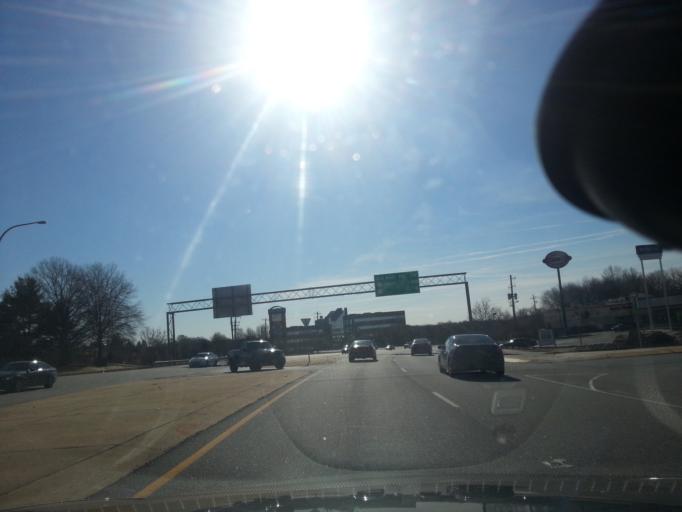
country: US
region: Delaware
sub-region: New Castle County
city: Bear
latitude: 39.6682
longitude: -75.6688
